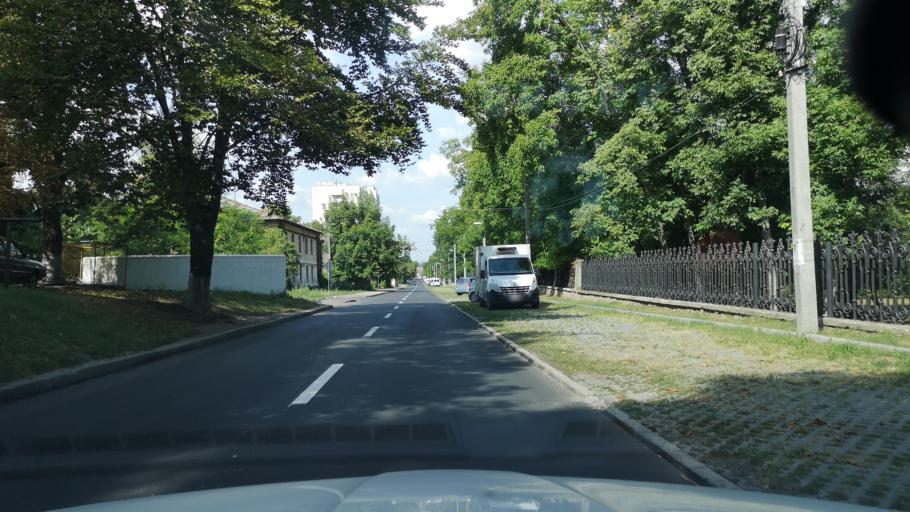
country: MD
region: Chisinau
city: Chisinau
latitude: 47.0247
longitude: 28.8090
